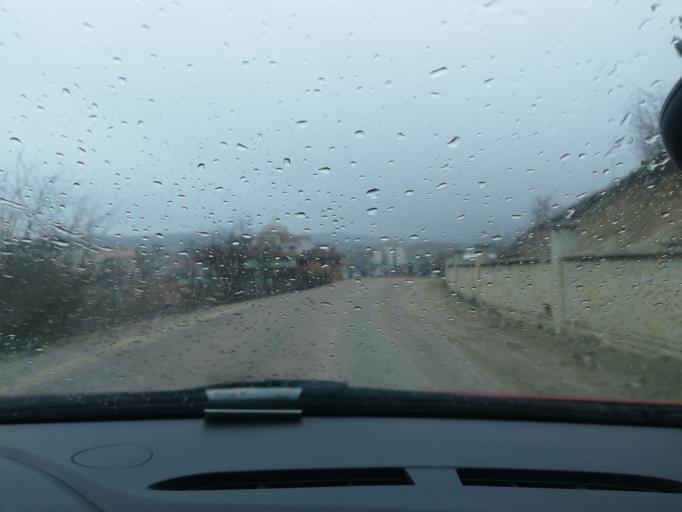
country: TR
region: Kastamonu
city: Seydiler
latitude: 41.6238
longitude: 33.7190
